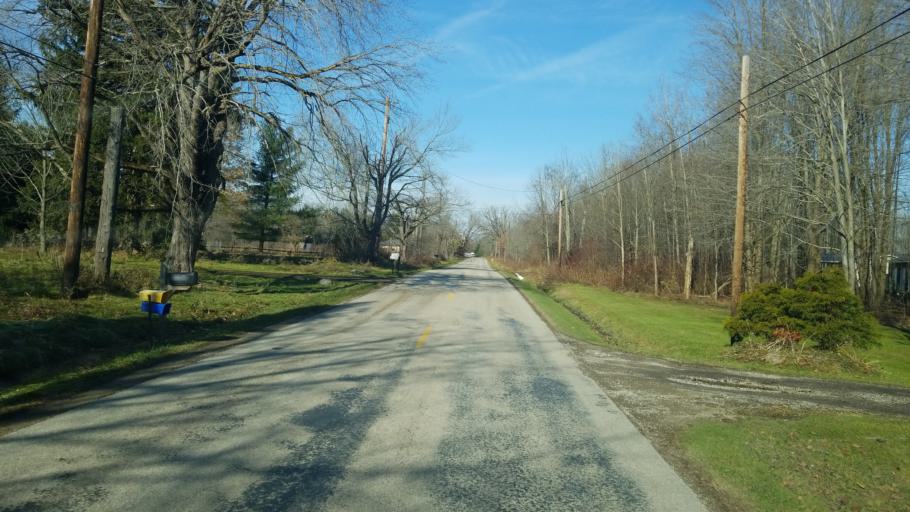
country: US
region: Ohio
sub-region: Ashtabula County
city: Jefferson
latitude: 41.7289
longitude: -80.7240
